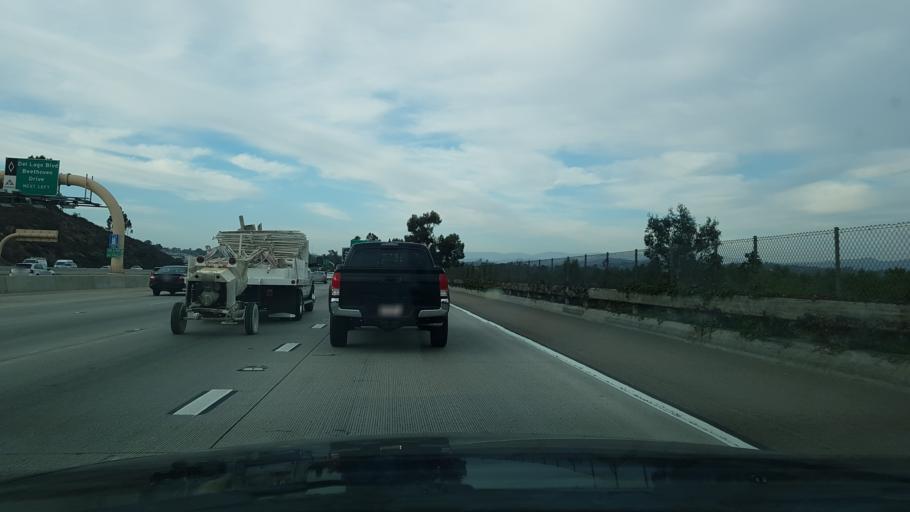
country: US
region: California
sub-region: San Diego County
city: Escondido
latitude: 33.0607
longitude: -117.0691
